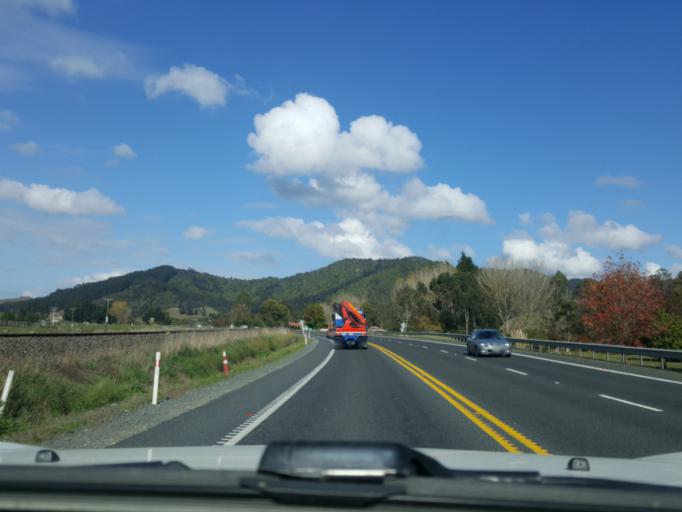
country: NZ
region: Waikato
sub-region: Waikato District
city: Ngaruawahia
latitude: -37.5904
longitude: 175.1593
